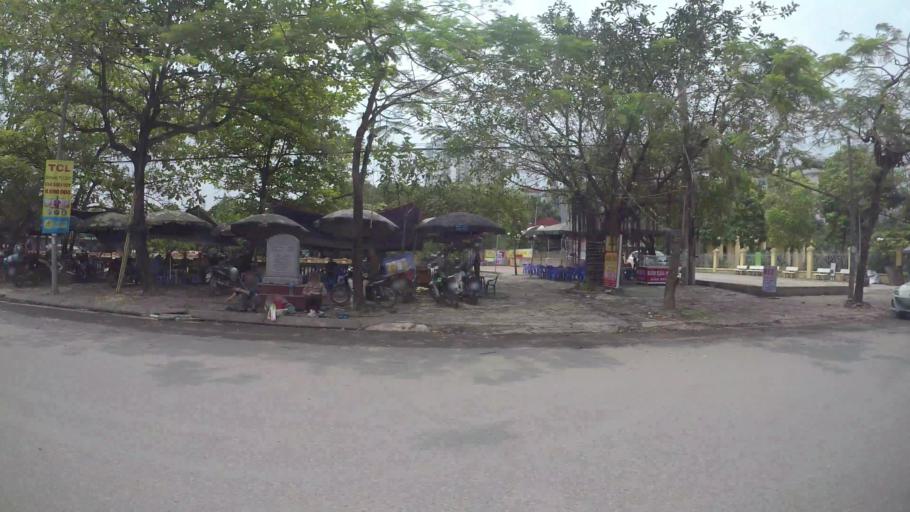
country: VN
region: Ha Noi
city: Tay Ho
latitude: 21.0665
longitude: 105.8045
